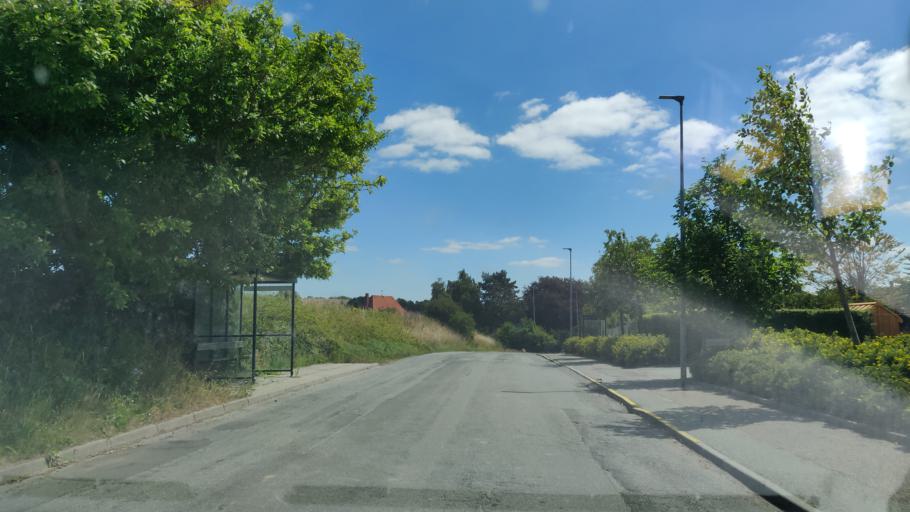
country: DK
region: South Denmark
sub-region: Kolding Kommune
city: Kolding
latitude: 55.5308
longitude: 9.5352
